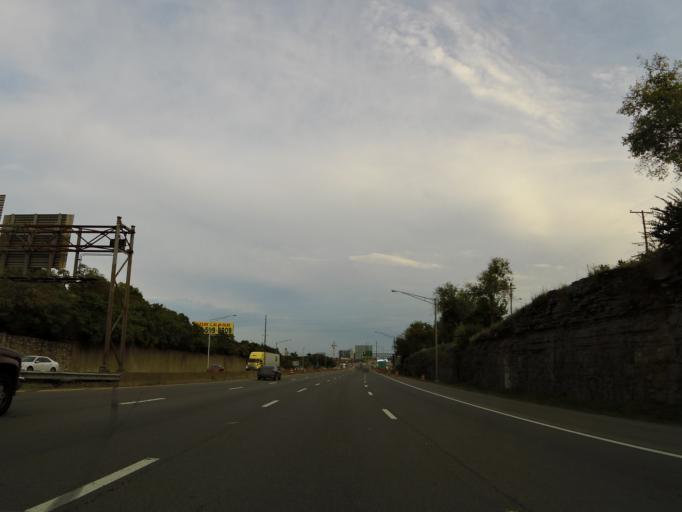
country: US
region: Tennessee
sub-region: Davidson County
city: Nashville
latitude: 36.1709
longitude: -86.7986
